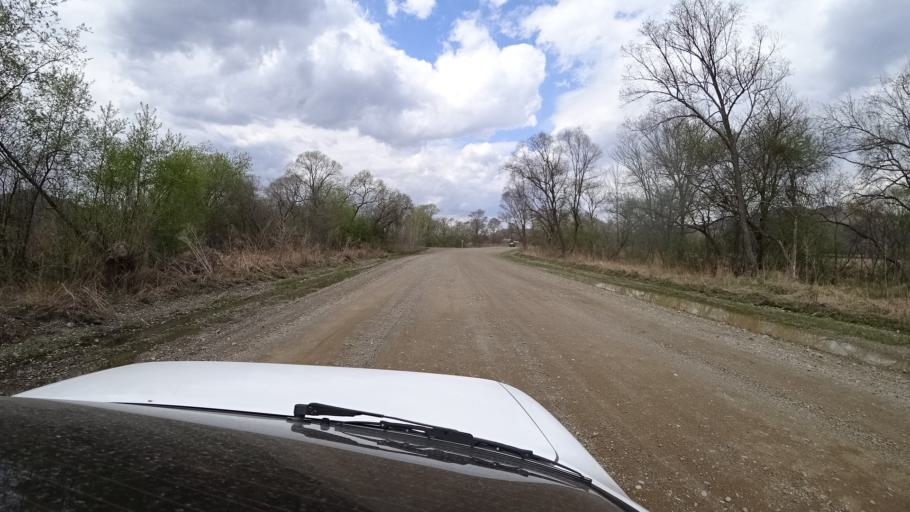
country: RU
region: Primorskiy
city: Novopokrovka
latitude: 45.6110
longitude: 134.2749
